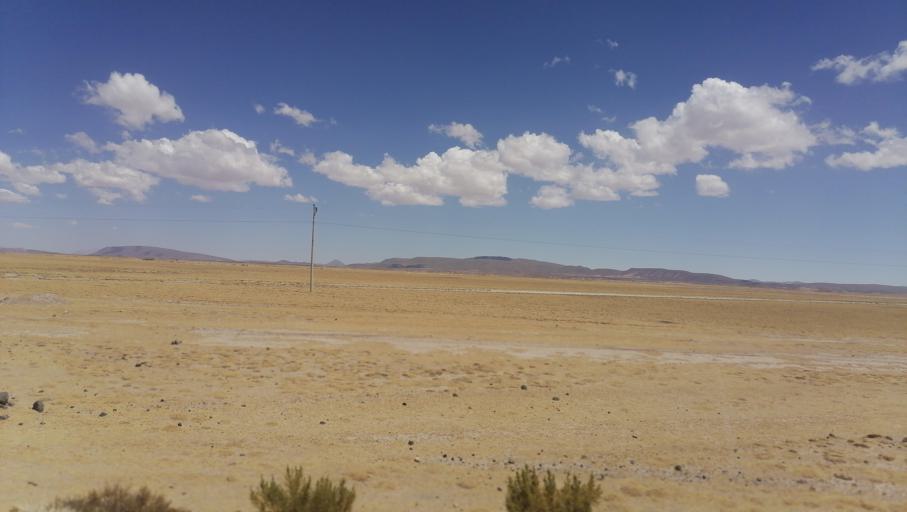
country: BO
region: Oruro
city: Challapata
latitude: -19.2188
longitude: -67.0002
